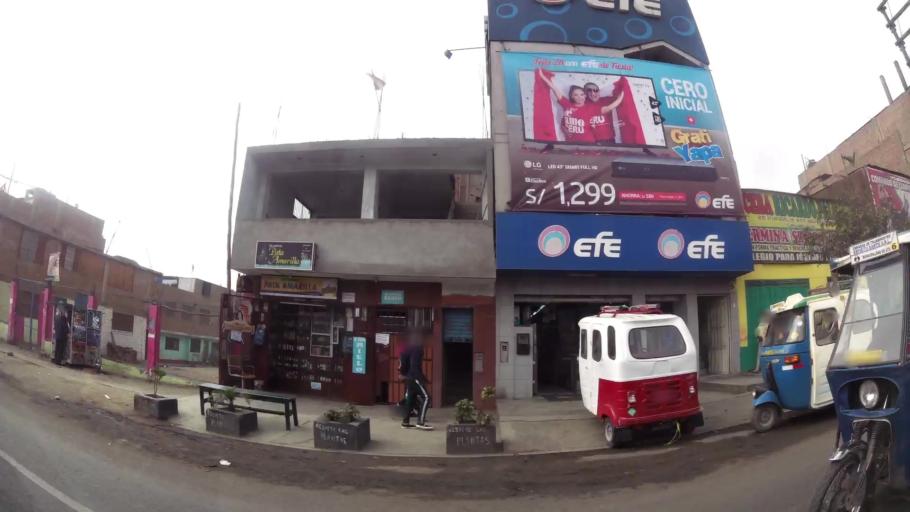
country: PE
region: Lima
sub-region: Lima
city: Chaclacayo
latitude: -12.0129
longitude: -76.8257
